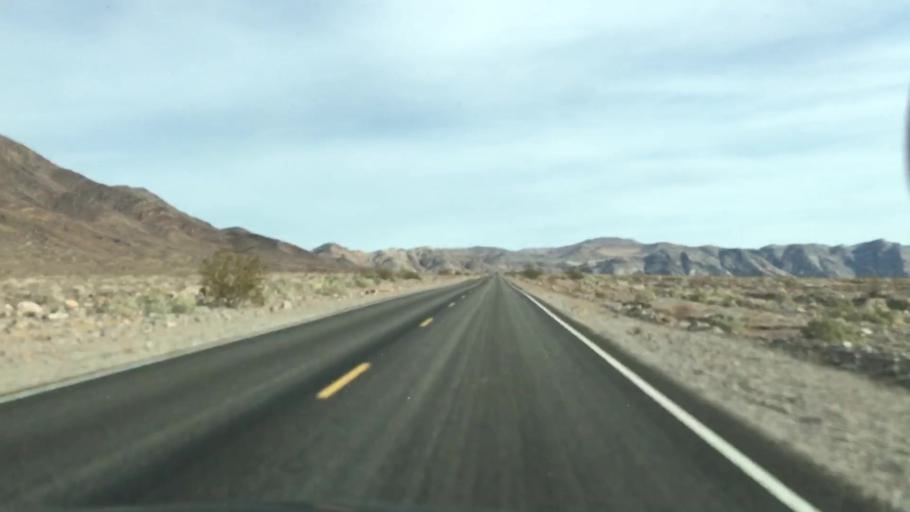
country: US
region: Nevada
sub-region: Nye County
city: Beatty
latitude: 36.7056
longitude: -116.9930
